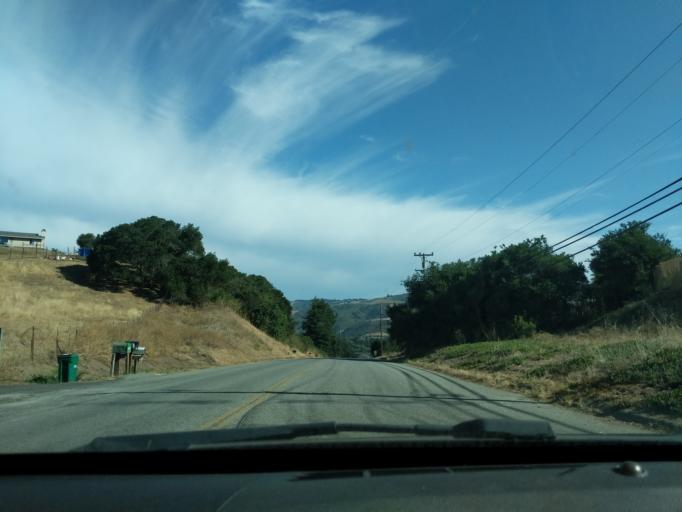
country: US
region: California
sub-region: San Benito County
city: Aromas
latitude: 36.8819
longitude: -121.6417
